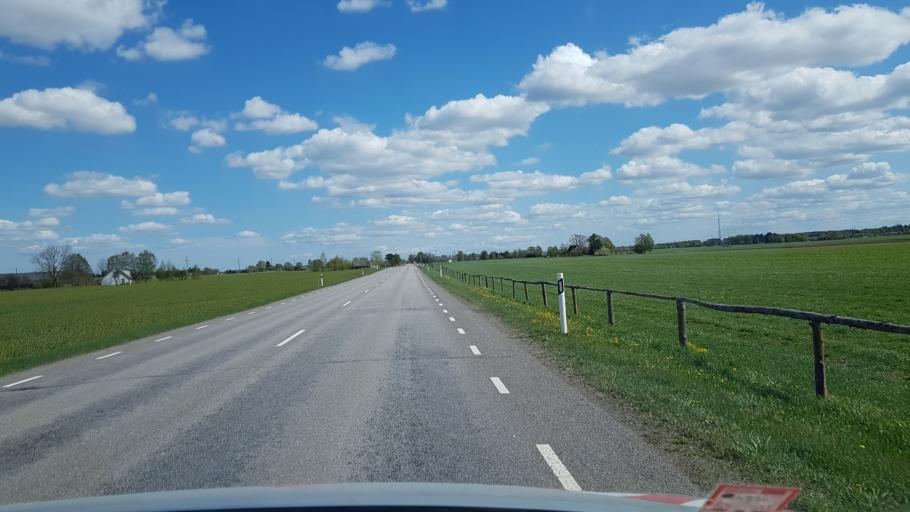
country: EE
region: Tartu
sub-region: Tartu linn
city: Tartu
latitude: 58.3806
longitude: 26.6347
